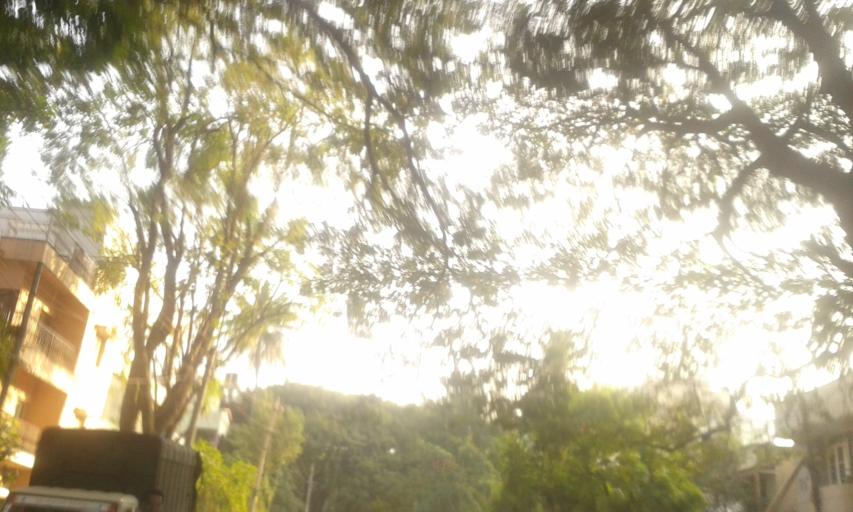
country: IN
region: Karnataka
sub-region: Bangalore Urban
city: Bangalore
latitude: 12.9203
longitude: 77.5953
